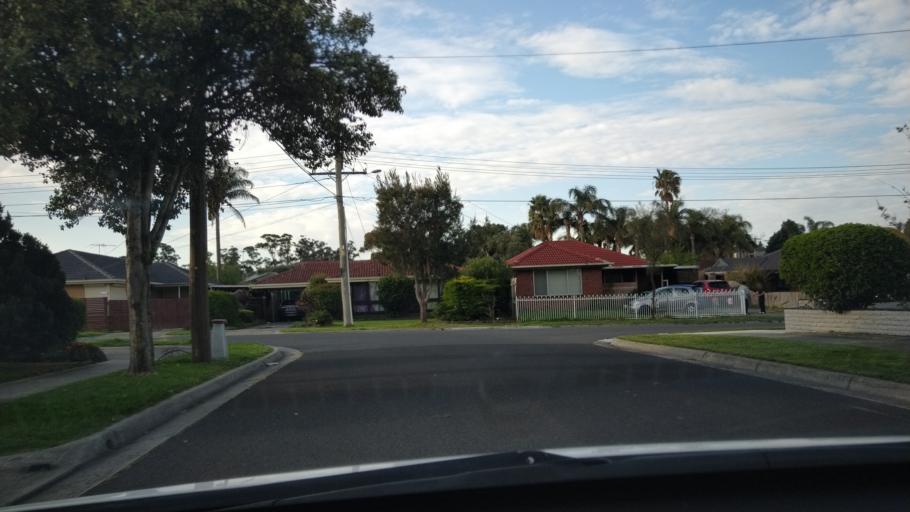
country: AU
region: Victoria
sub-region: Greater Dandenong
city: Springvale South
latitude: -37.9677
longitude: 145.1521
